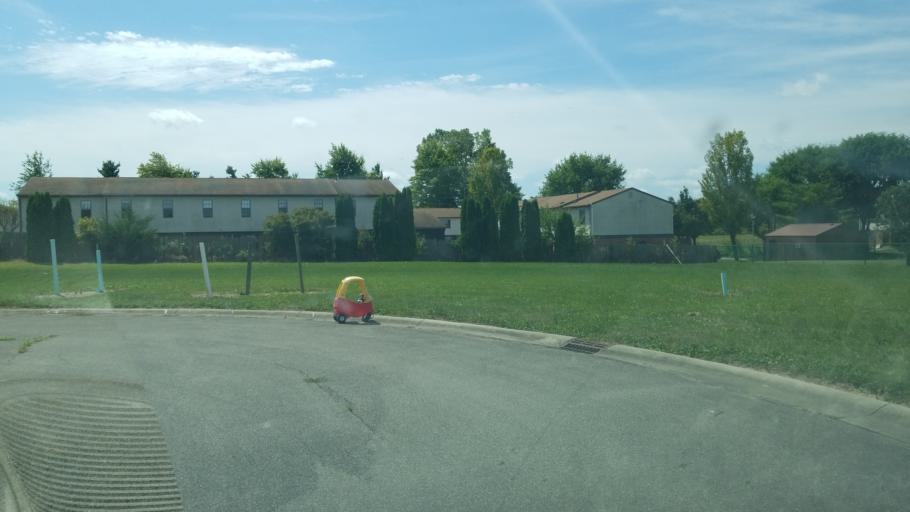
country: US
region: Ohio
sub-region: Hardin County
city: Kenton
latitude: 40.6409
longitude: -83.5947
